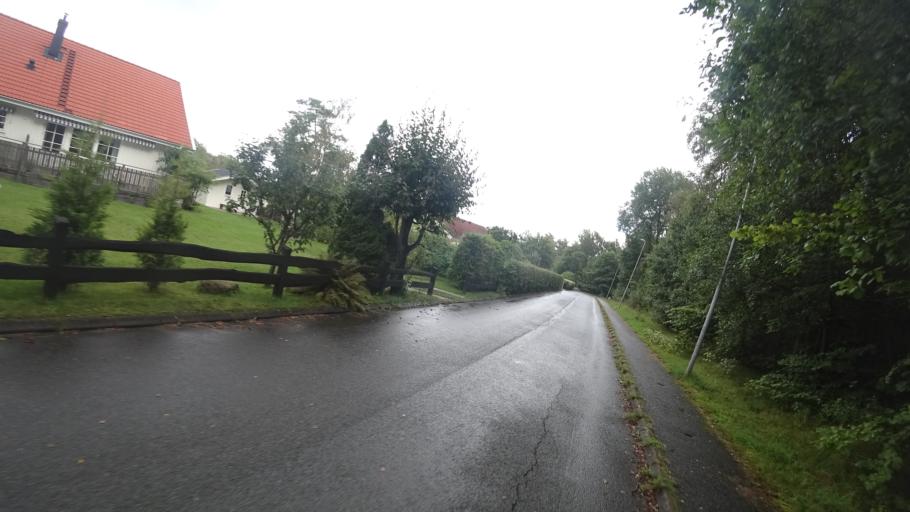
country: SE
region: Vaestra Goetaland
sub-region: Partille Kommun
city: Furulund
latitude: 57.7012
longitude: 12.1371
